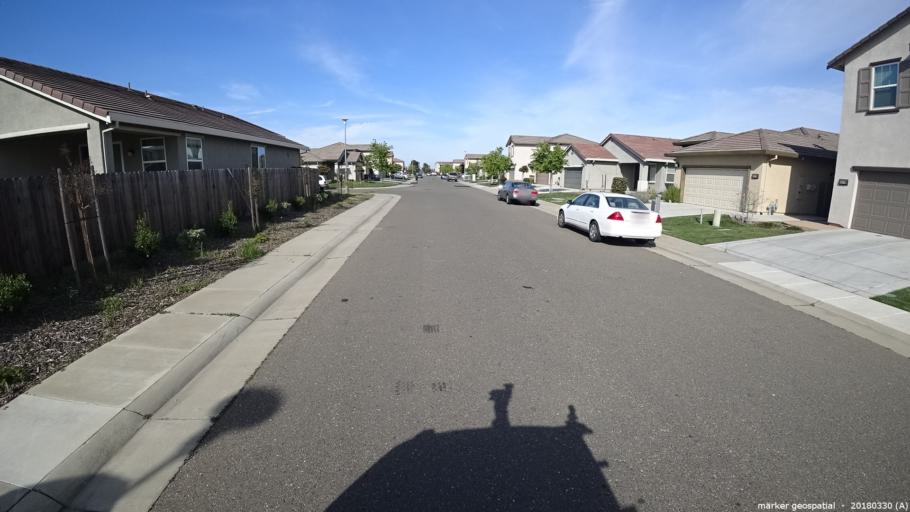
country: US
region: California
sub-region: Sacramento County
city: Vineyard
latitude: 38.4828
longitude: -121.3420
